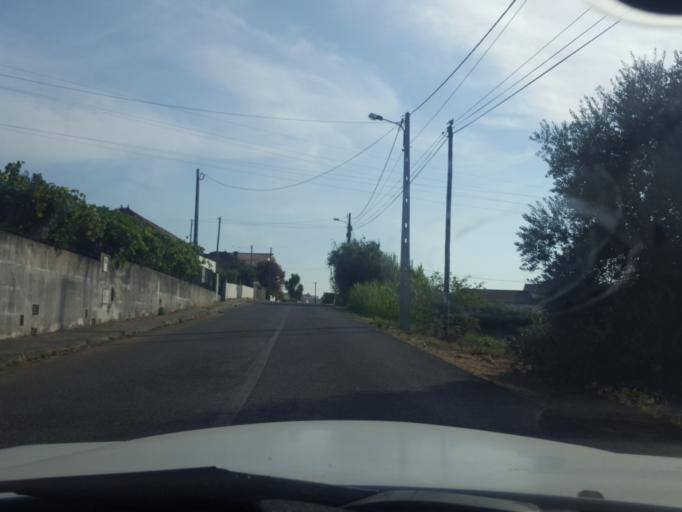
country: PT
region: Leiria
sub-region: Leiria
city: Leiria
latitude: 39.7170
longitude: -8.7842
